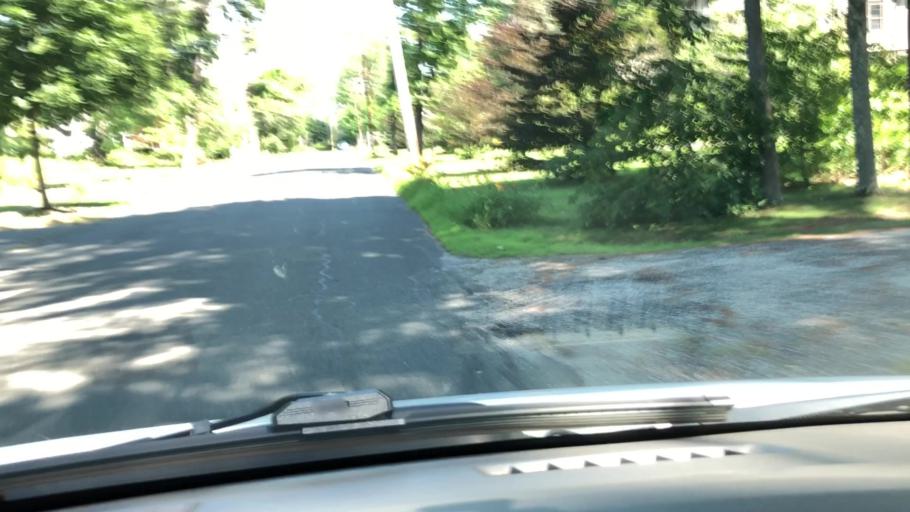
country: US
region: Massachusetts
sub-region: Hampshire County
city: Northampton
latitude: 42.3318
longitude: -72.6666
